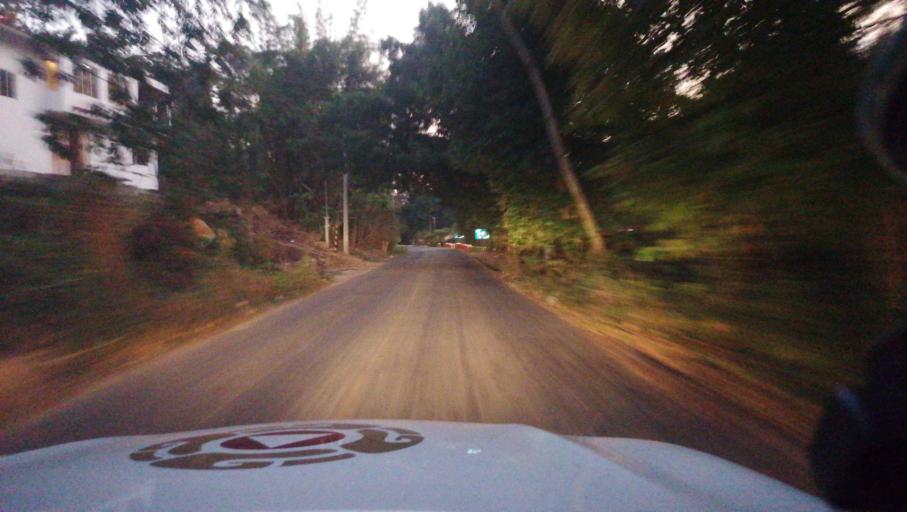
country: MX
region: Chiapas
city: Veinte de Noviembre
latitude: 14.9626
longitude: -92.2533
